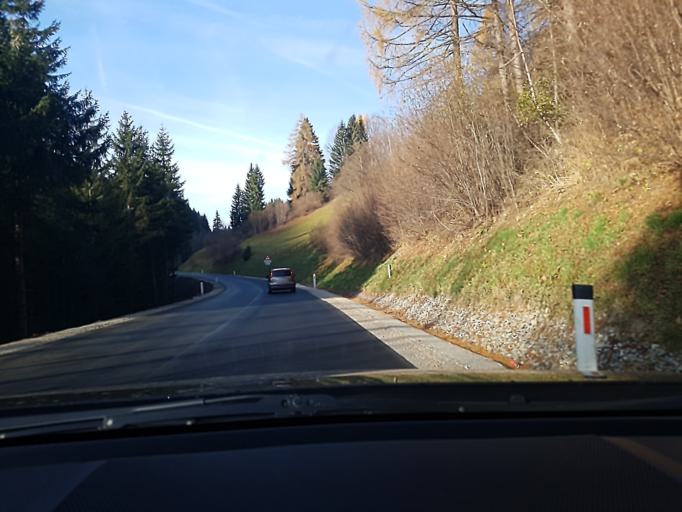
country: AT
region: Styria
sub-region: Politischer Bezirk Murau
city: Krakauhintermuhlen
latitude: 47.1649
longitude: 13.9916
